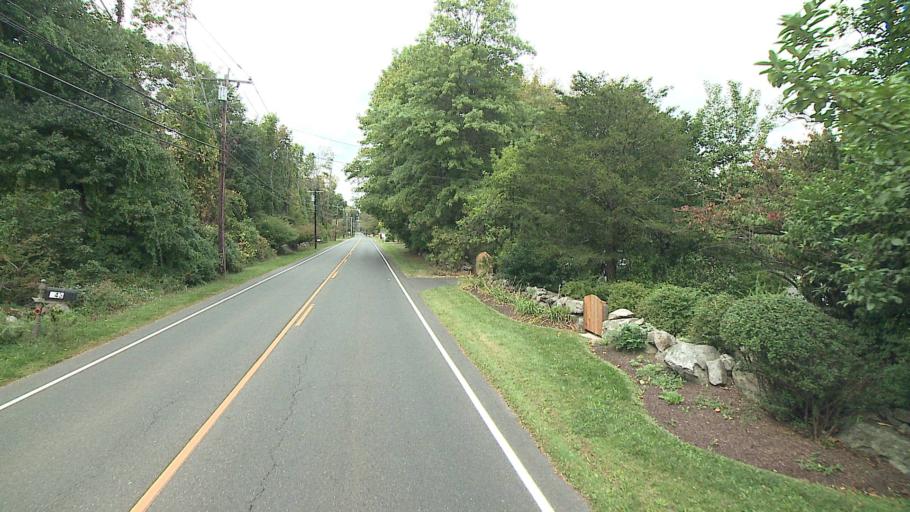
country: US
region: Connecticut
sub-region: Fairfield County
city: Wilton
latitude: 41.2234
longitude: -73.4768
